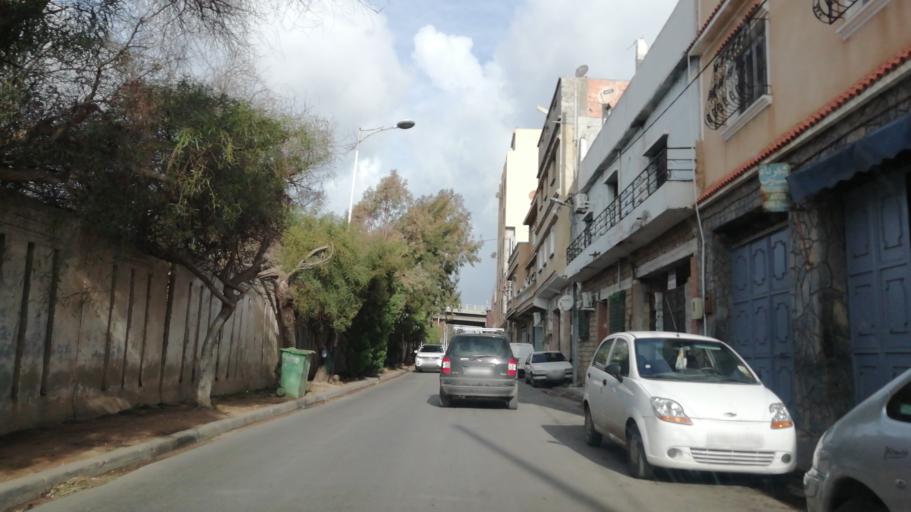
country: DZ
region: Oran
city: Oran
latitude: 35.6840
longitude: -0.6281
